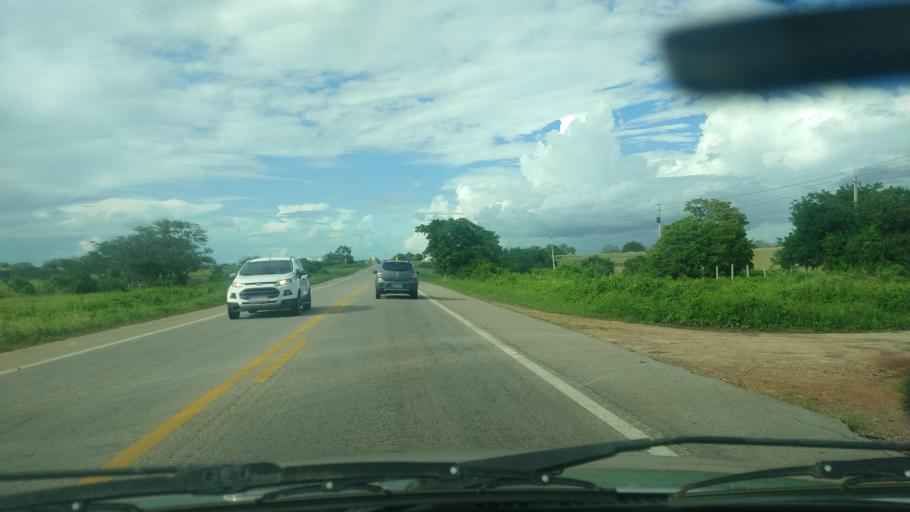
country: BR
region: Rio Grande do Norte
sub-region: Tangara
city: Tangara
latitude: -6.1779
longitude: -35.7690
